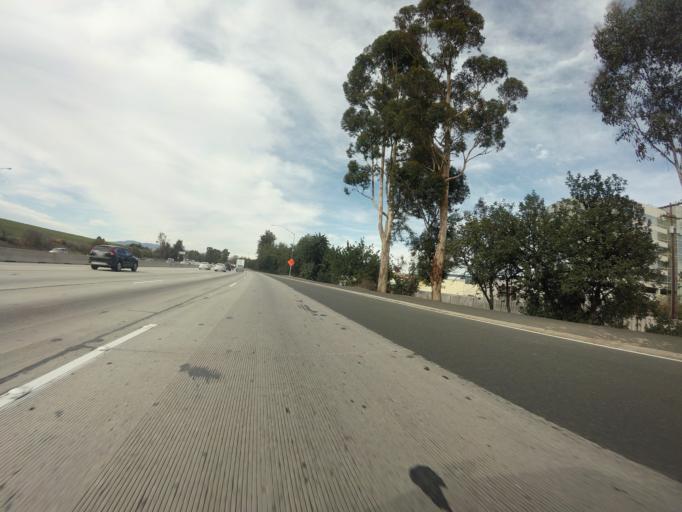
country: US
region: California
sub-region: Los Angeles County
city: Van Nuys
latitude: 34.1758
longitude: -118.4677
